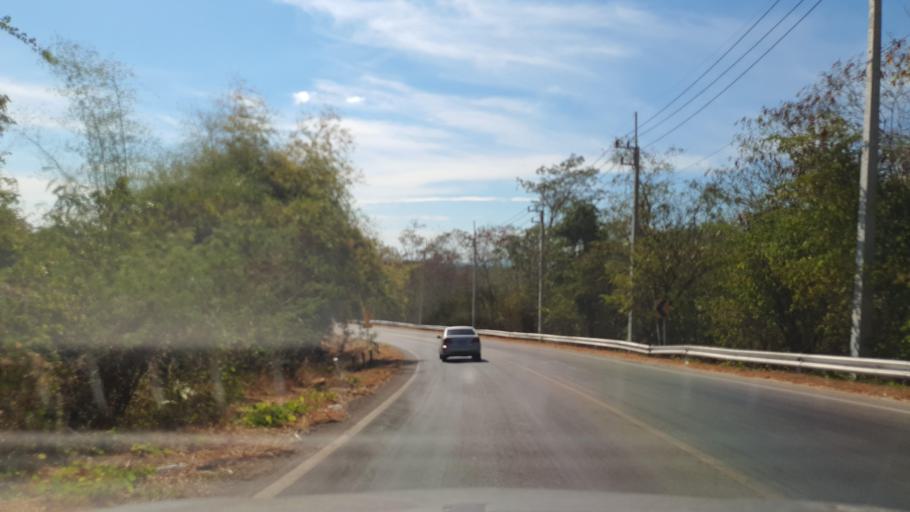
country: TH
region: Kalasin
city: Khao Wong
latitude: 16.7537
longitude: 104.1204
